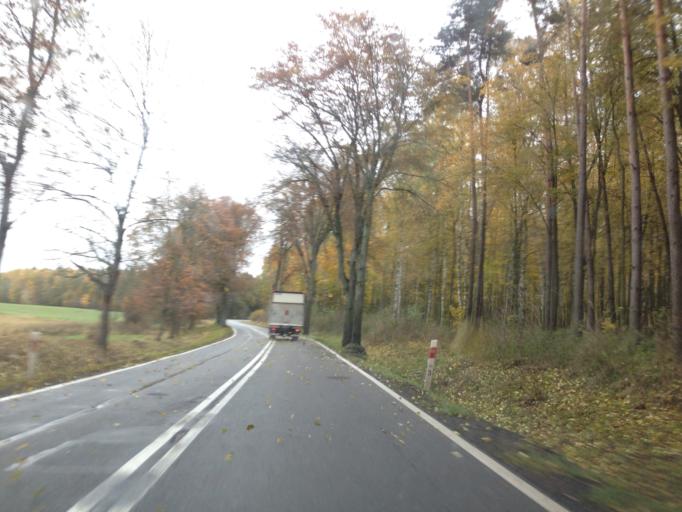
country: PL
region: Pomeranian Voivodeship
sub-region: Powiat kwidzynski
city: Ryjewo
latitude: 53.8476
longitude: 18.9996
